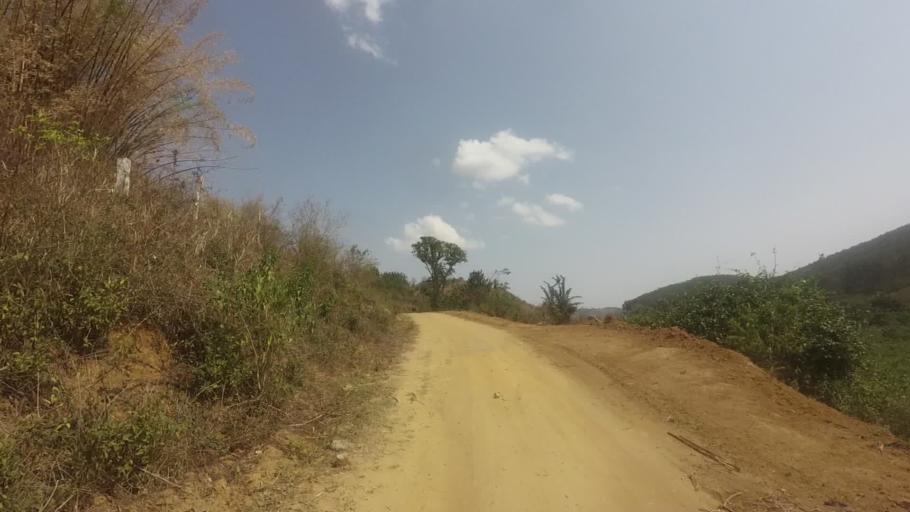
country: BR
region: Espirito Santo
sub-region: Sao Jose Do Calcado
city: Sao Jose do Calcado
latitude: -21.0178
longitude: -41.5159
